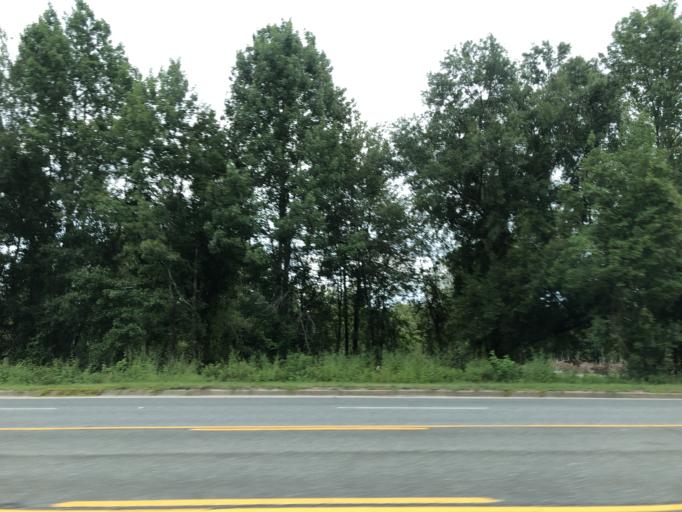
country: US
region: Georgia
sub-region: Wayne County
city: Jesup
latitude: 31.6153
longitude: -81.8905
